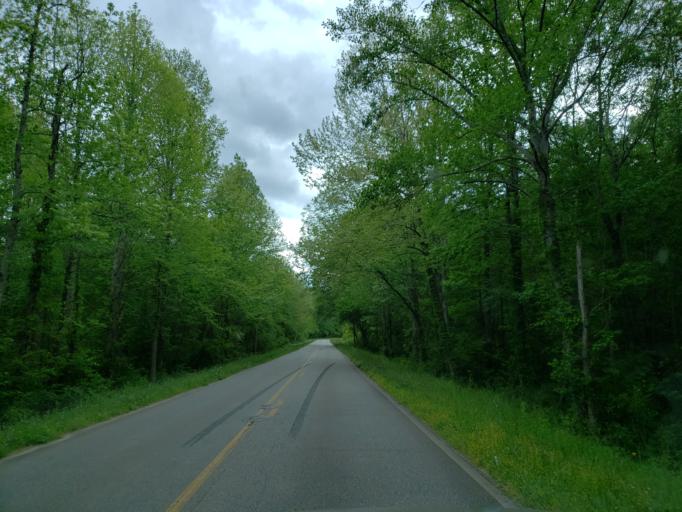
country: US
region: Georgia
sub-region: Haralson County
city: Tallapoosa
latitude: 33.7689
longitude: -85.3375
